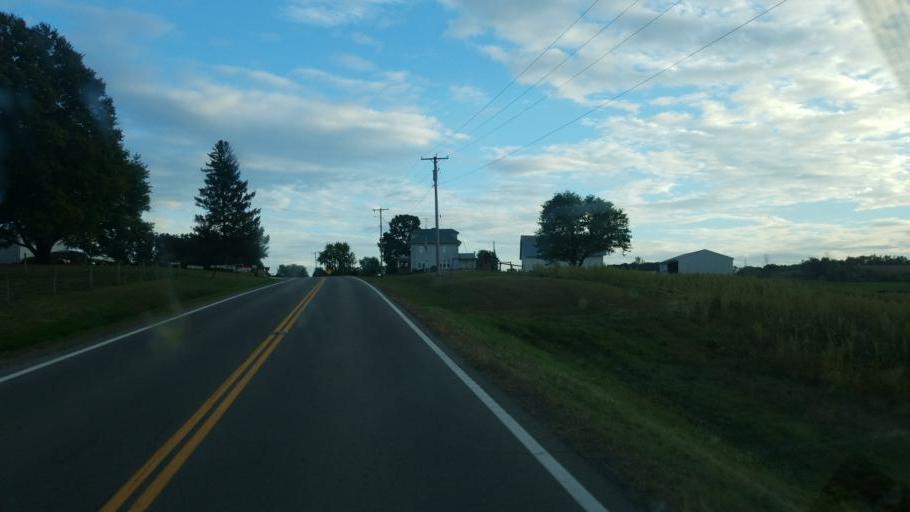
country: US
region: Ohio
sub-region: Ashland County
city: Loudonville
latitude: 40.6634
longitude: -82.2310
